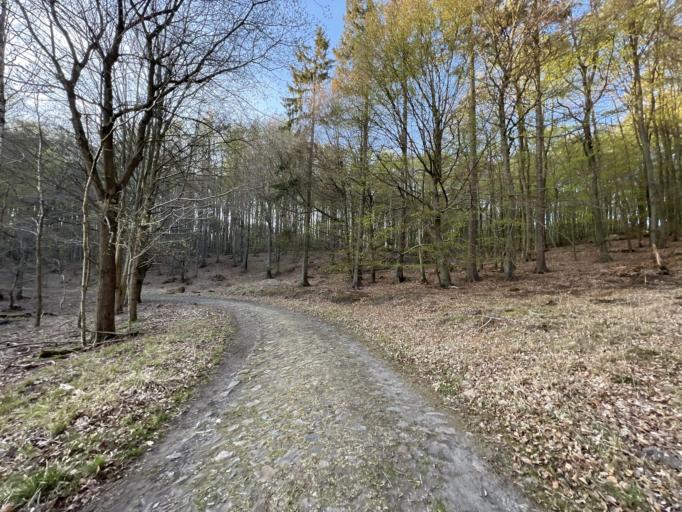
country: DE
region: Mecklenburg-Vorpommern
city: Sassnitz
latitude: 54.5369
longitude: 13.6584
